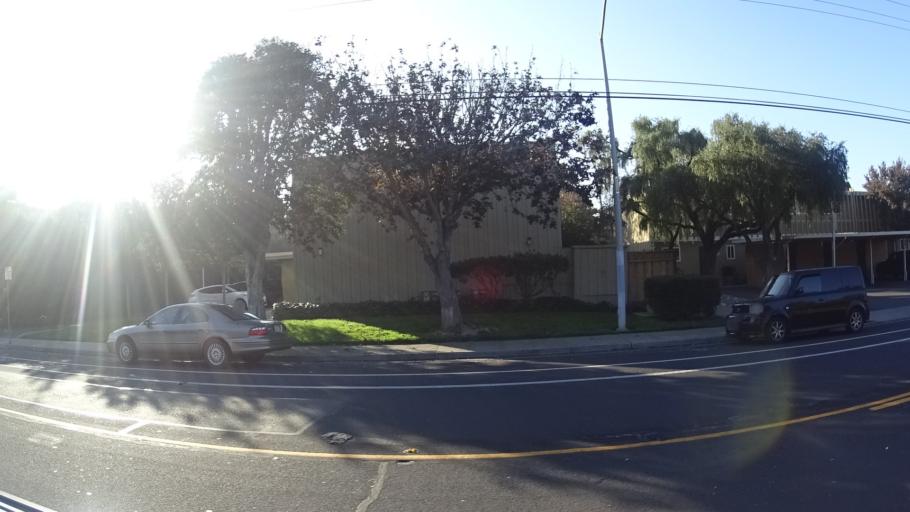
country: US
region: California
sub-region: Santa Clara County
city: Santa Clara
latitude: 37.3386
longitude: -121.9875
